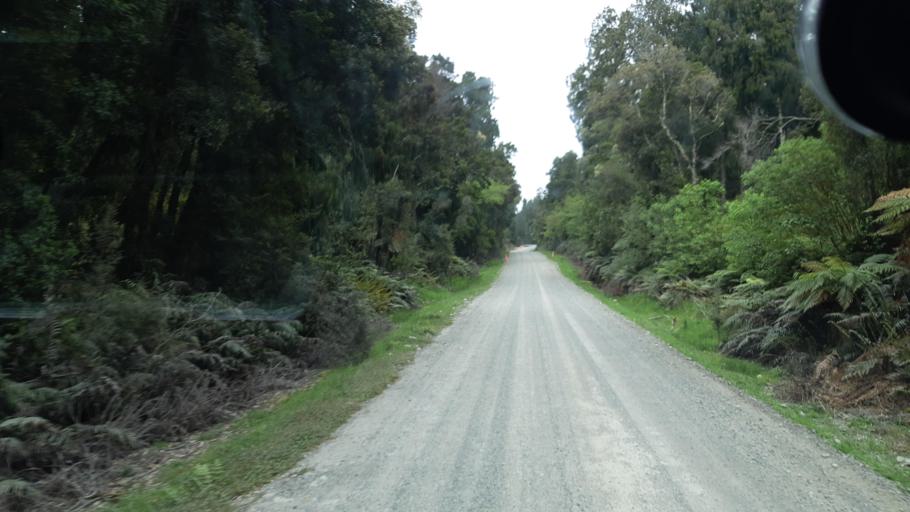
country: NZ
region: West Coast
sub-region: Grey District
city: Greymouth
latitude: -42.6470
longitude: 171.3288
